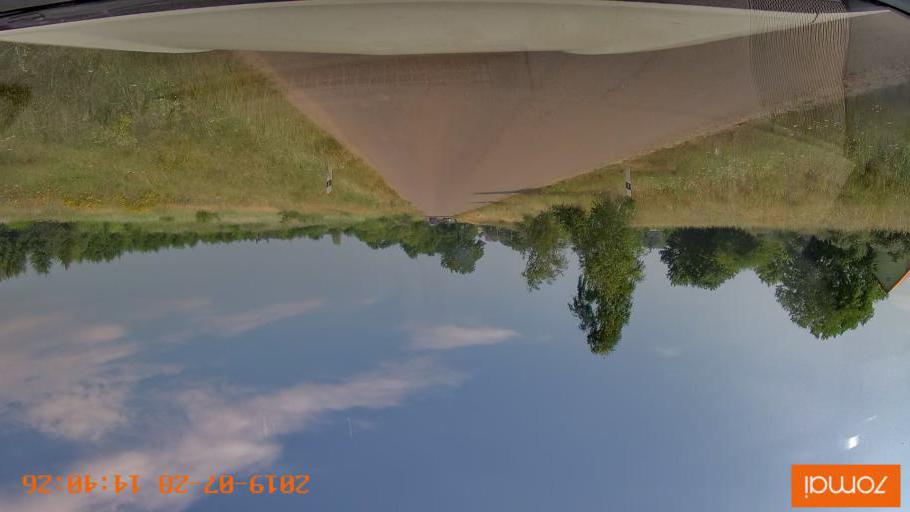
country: RU
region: Kaliningrad
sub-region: Gorod Kaliningrad
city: Yantarnyy
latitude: 54.8515
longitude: 19.9578
